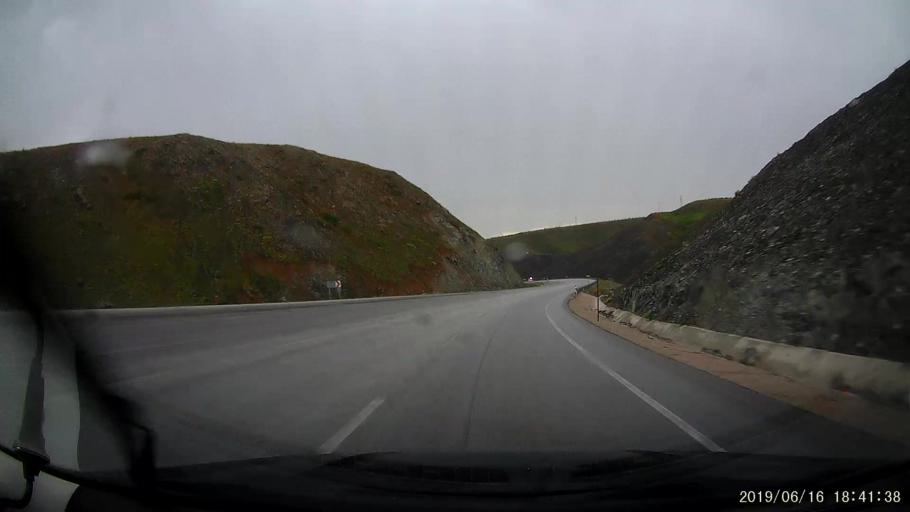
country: TR
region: Erzincan
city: Doganbeyli
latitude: 39.8722
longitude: 39.1251
